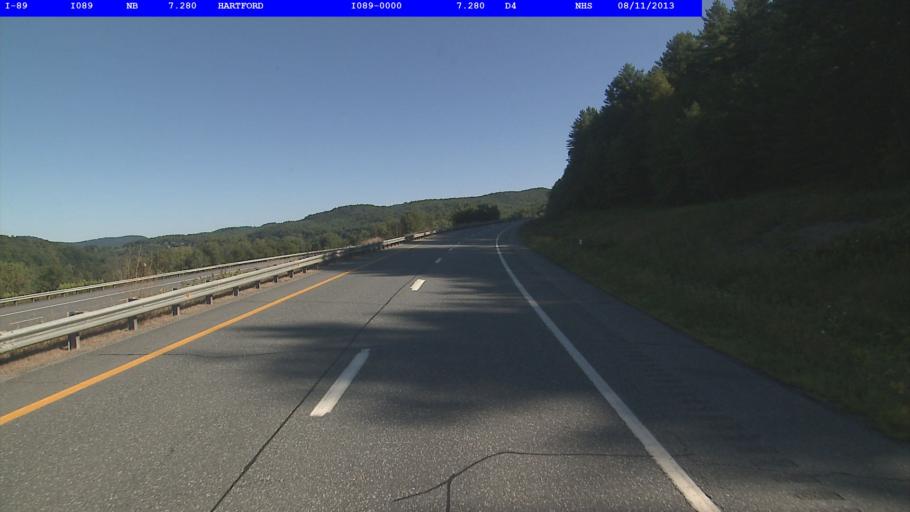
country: US
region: Vermont
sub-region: Windsor County
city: Wilder
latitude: 43.7094
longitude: -72.4138
